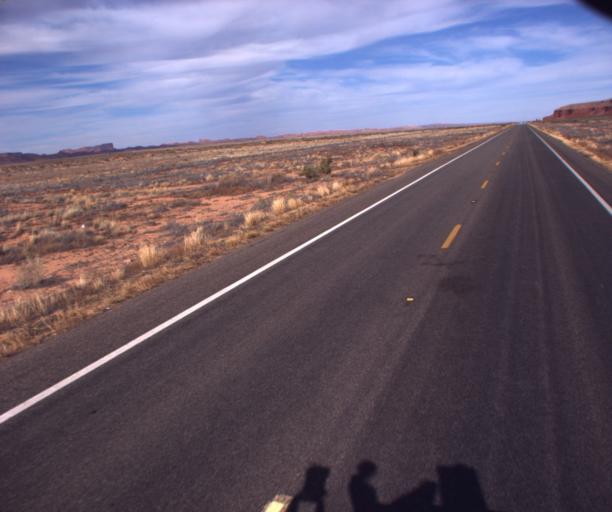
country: US
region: Arizona
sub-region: Navajo County
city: Kayenta
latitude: 36.7531
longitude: -110.0575
